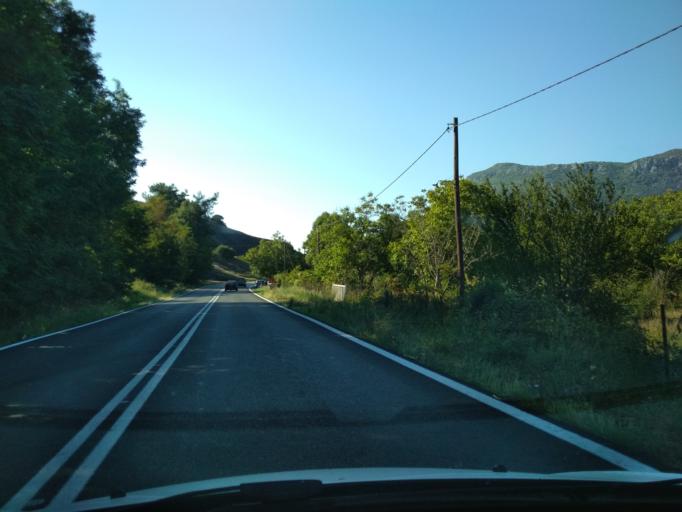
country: GR
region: Thessaly
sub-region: Trikala
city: Kastraki
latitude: 39.7063
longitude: 21.6113
